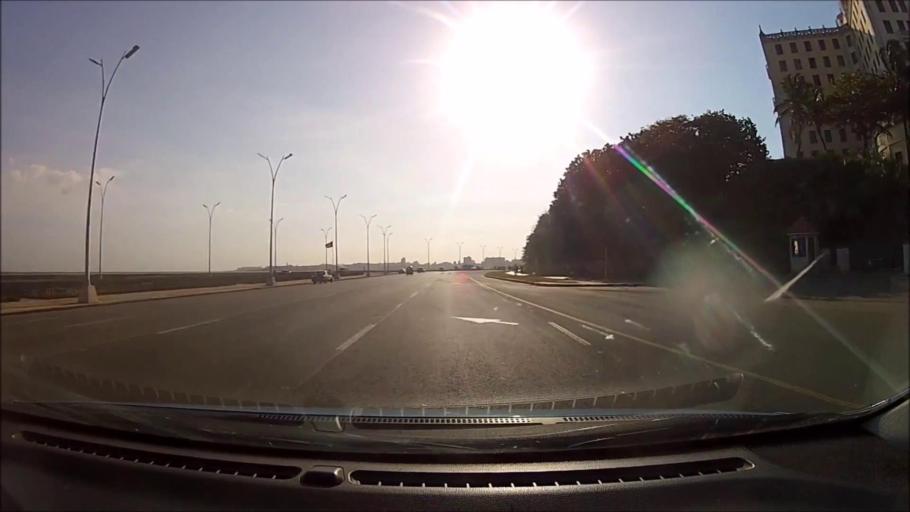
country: CU
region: La Habana
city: Havana
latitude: 23.1441
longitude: -82.3803
